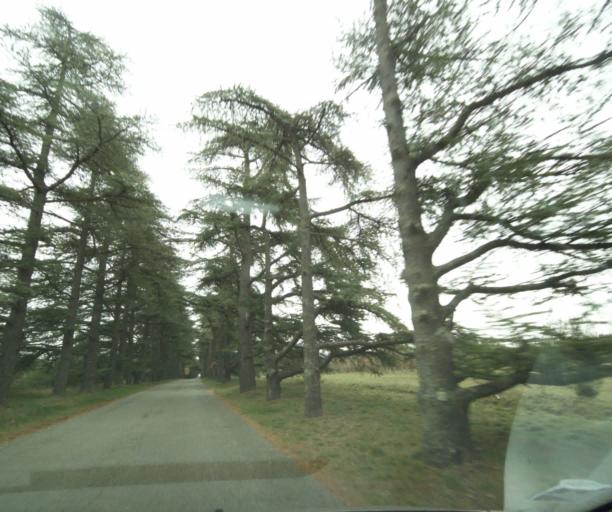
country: FR
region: Provence-Alpes-Cote d'Azur
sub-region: Departement du Var
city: Vinon-sur-Verdon
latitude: 43.7148
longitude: 5.7533
